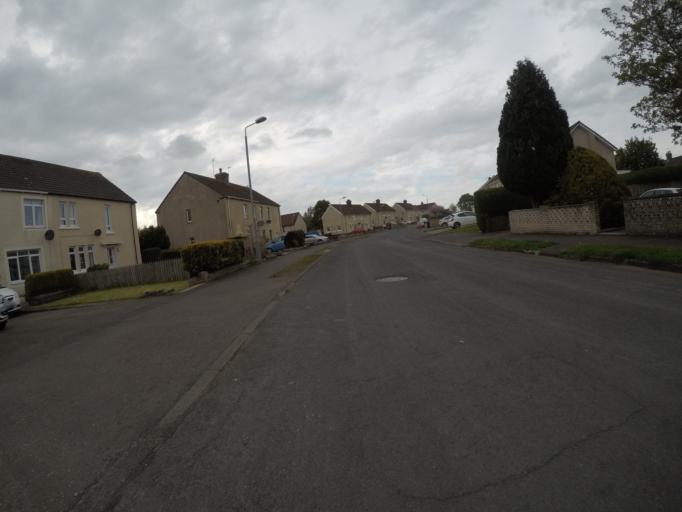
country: GB
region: Scotland
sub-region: East Ayrshire
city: Kilmaurs
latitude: 55.6405
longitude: -4.5334
